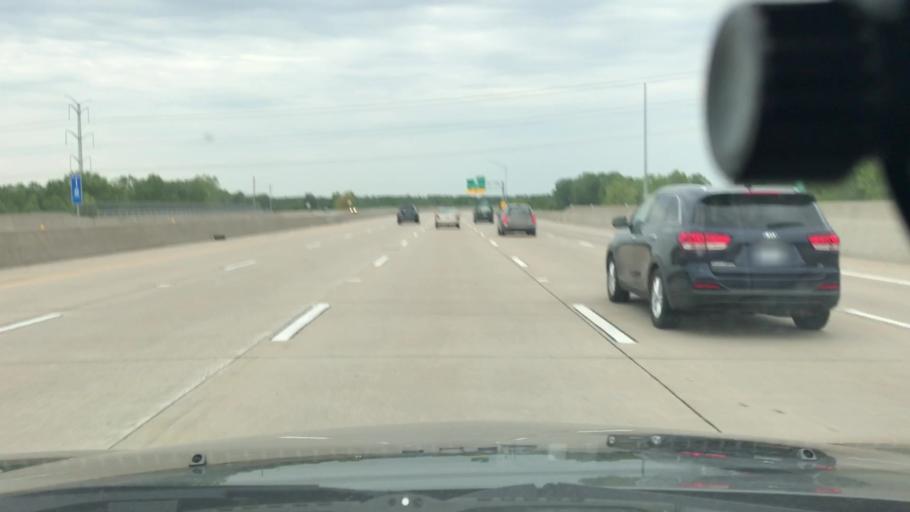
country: US
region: Missouri
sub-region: Saint Louis County
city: Maryland Heights
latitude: 38.7066
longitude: -90.4946
